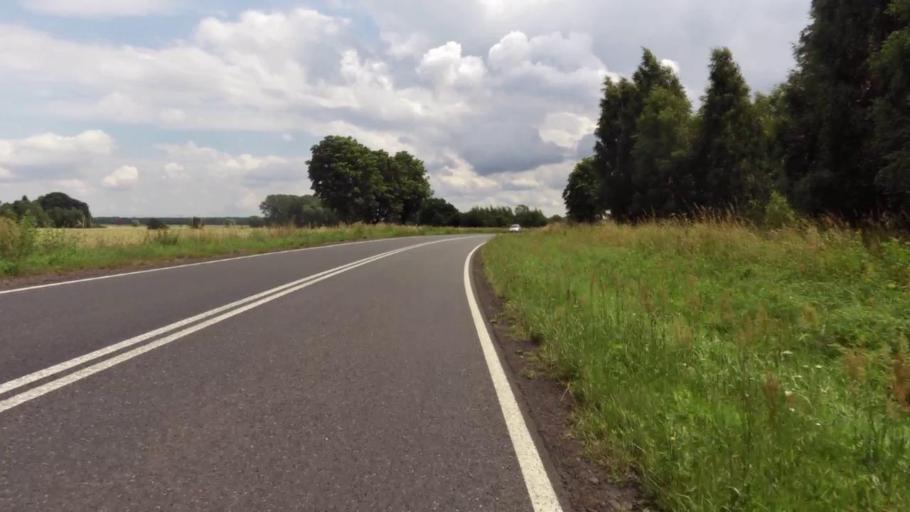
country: PL
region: West Pomeranian Voivodeship
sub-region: Powiat pyrzycki
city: Lipiany
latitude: 52.9983
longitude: 15.0402
